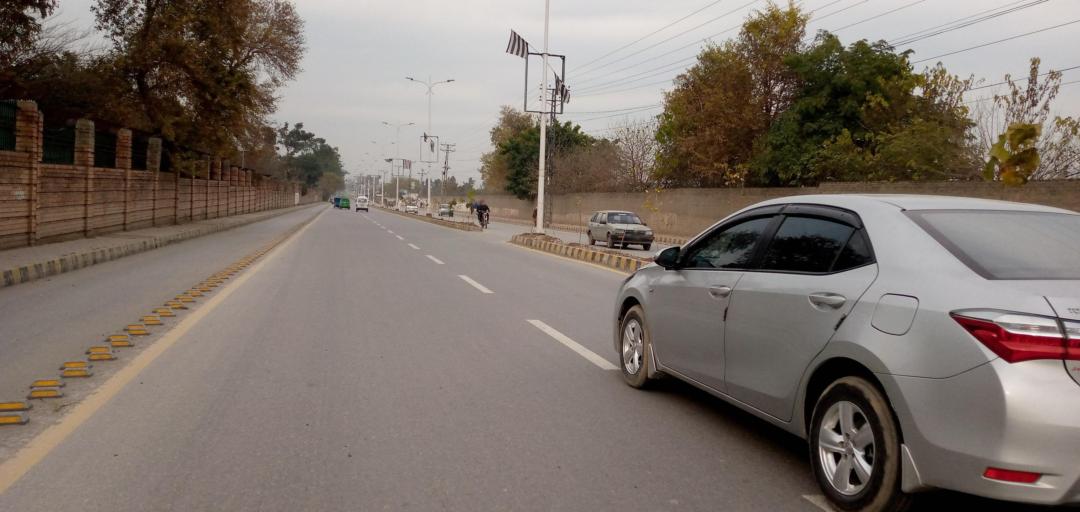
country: PK
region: Khyber Pakhtunkhwa
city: Peshawar
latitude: 34.0110
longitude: 71.4890
